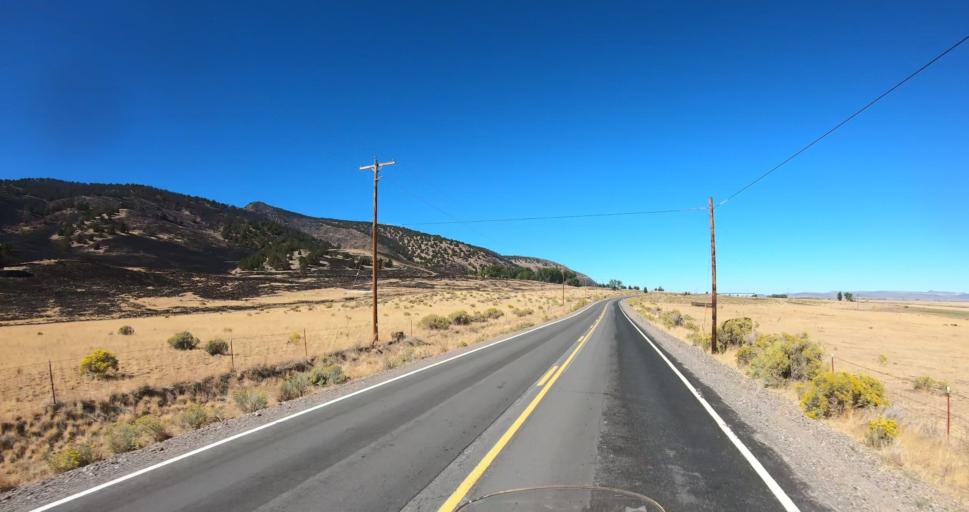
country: US
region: Oregon
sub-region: Lake County
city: Lakeview
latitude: 42.6371
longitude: -120.5188
